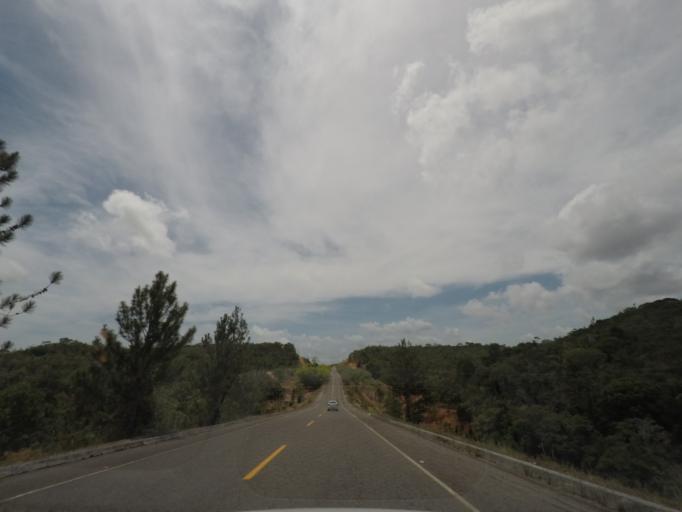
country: BR
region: Bahia
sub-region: Conde
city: Conde
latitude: -11.9151
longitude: -37.6609
